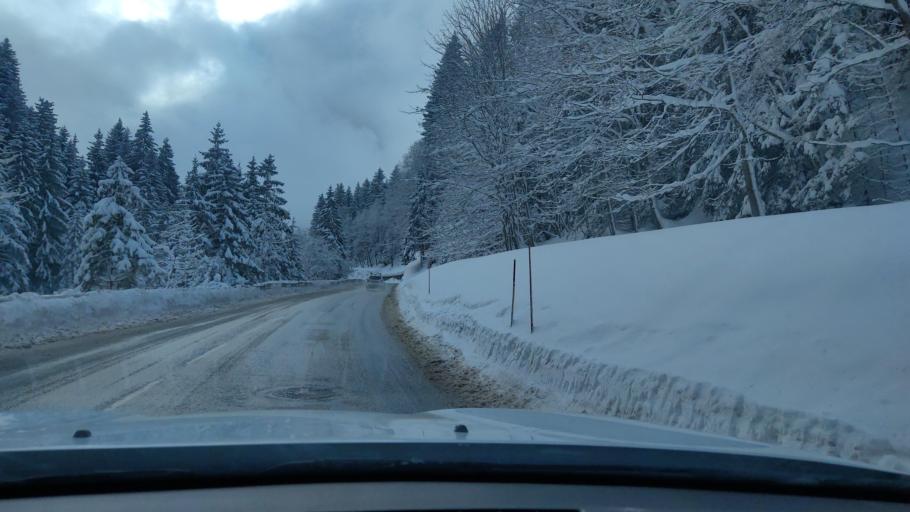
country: FR
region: Rhone-Alpes
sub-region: Departement de la Savoie
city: Courchevel
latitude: 45.3902
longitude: 6.7130
